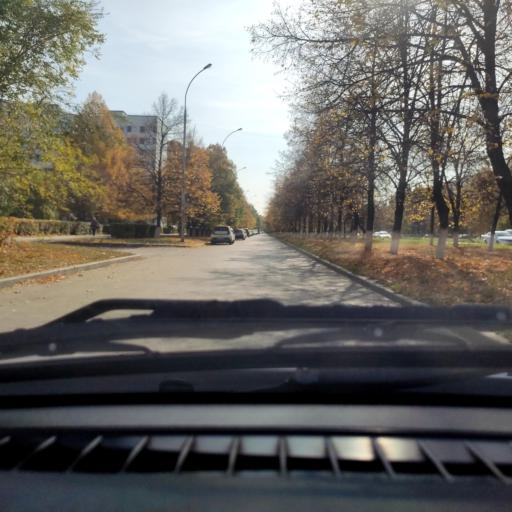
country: RU
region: Samara
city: Tol'yatti
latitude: 53.5231
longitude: 49.3115
